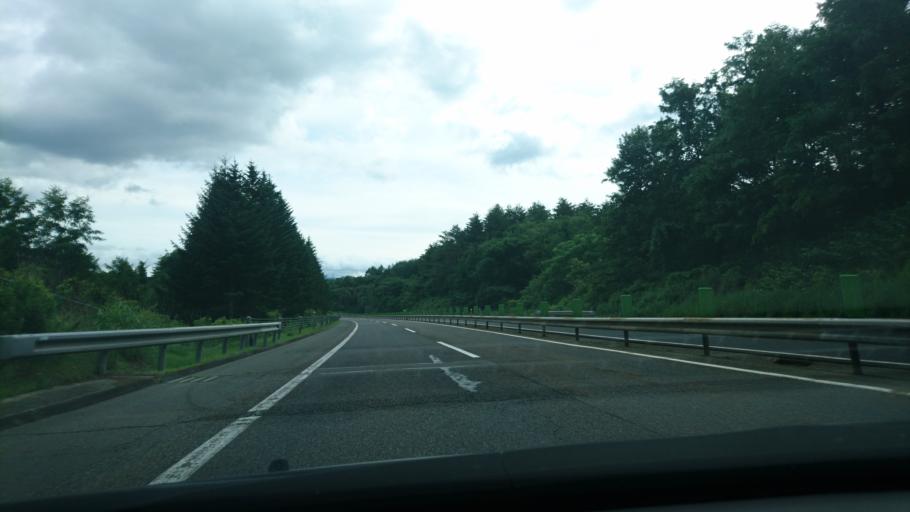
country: JP
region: Aomori
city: Hachinohe
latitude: 40.4289
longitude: 141.4410
